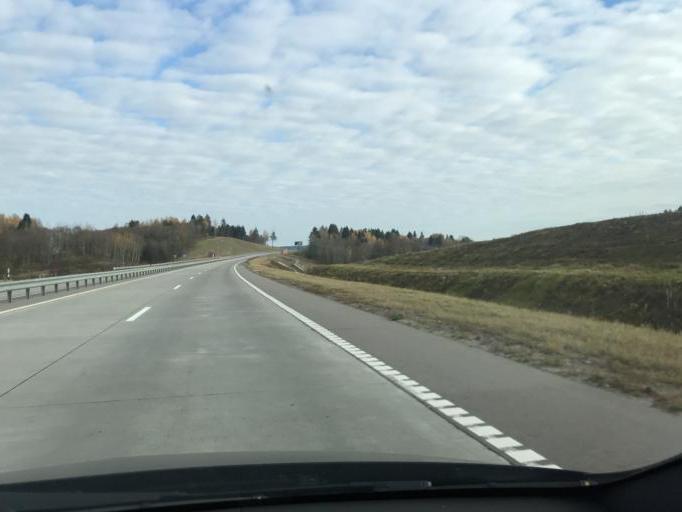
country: BY
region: Minsk
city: Pyatryshki
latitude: 54.0490
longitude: 27.1848
